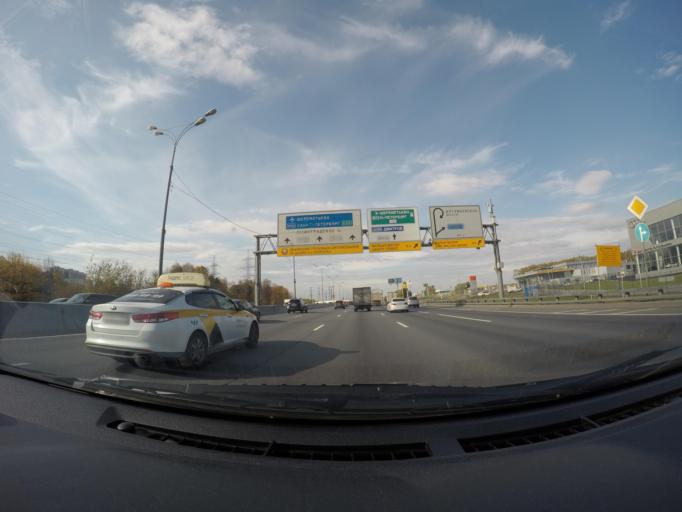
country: RU
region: Moscow
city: Lianozovo
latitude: 55.9071
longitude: 37.5989
